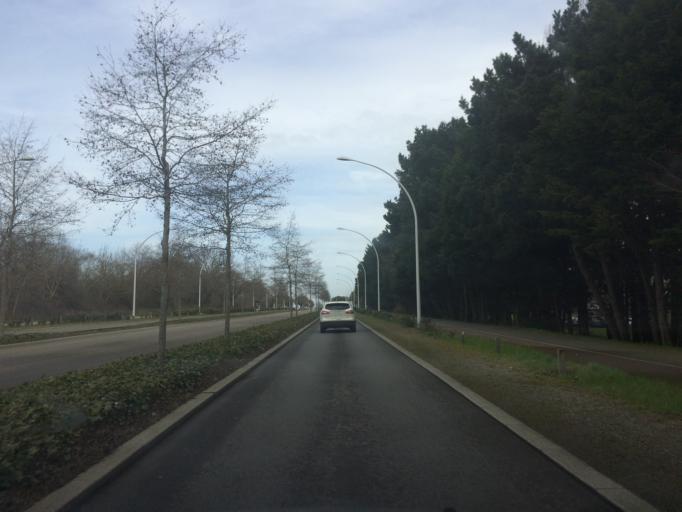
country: FR
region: Pays de la Loire
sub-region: Departement de la Loire-Atlantique
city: Saint-Nazaire
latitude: 47.2621
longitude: -2.2612
